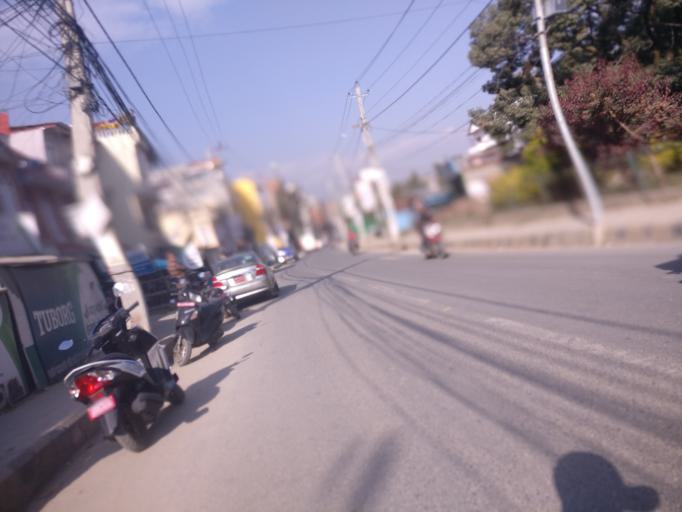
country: NP
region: Central Region
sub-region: Bagmati Zone
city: Patan
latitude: 27.6754
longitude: 85.3081
